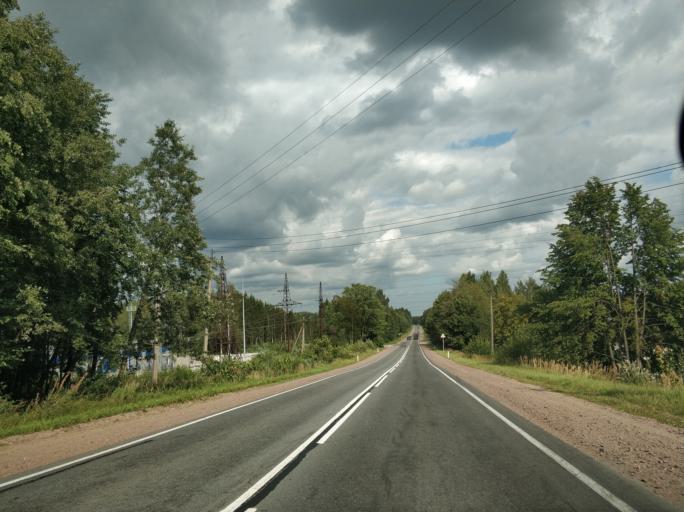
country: RU
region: Leningrad
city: Romanovka
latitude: 60.0708
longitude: 30.7440
